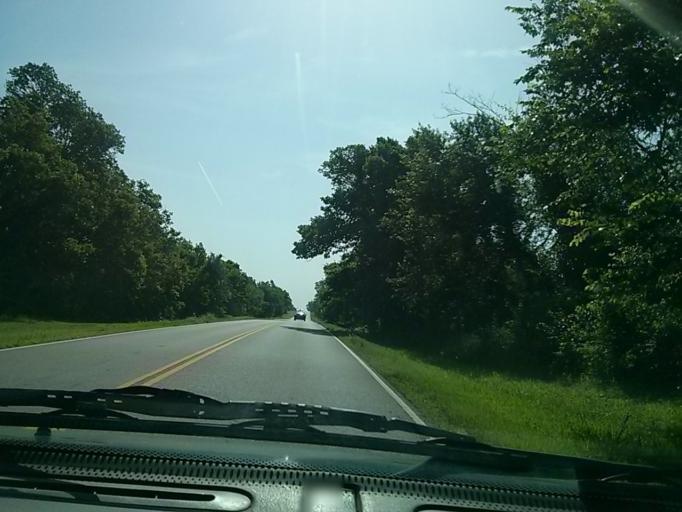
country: US
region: Oklahoma
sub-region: Rogers County
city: Catoosa
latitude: 36.1334
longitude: -95.8041
